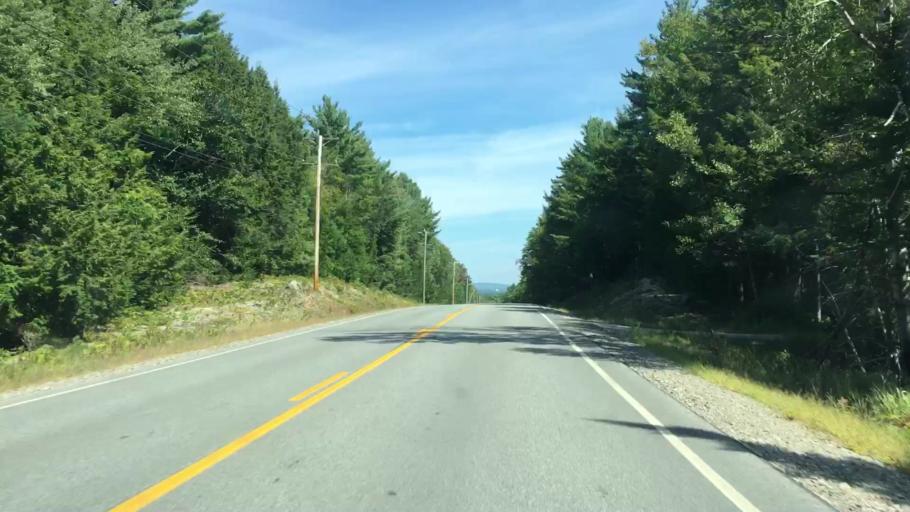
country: US
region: Maine
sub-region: Penobscot County
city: Howland
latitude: 45.2332
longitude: -68.7537
